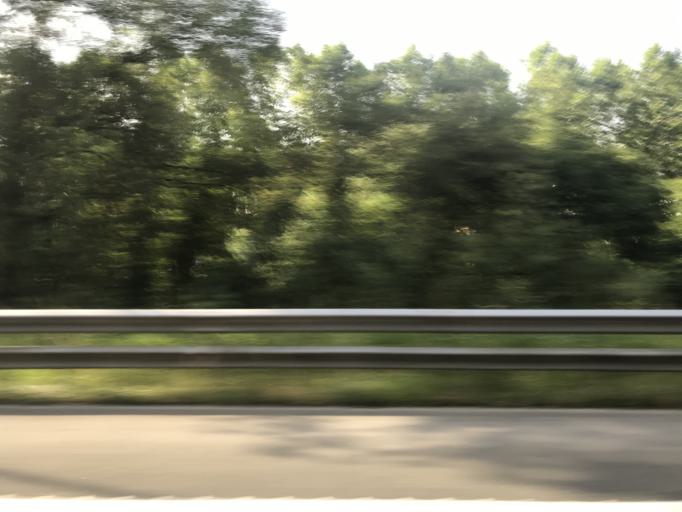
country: ES
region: Basque Country
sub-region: Provincia de Guipuzcoa
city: Andoain
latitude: 43.2138
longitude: -2.0262
